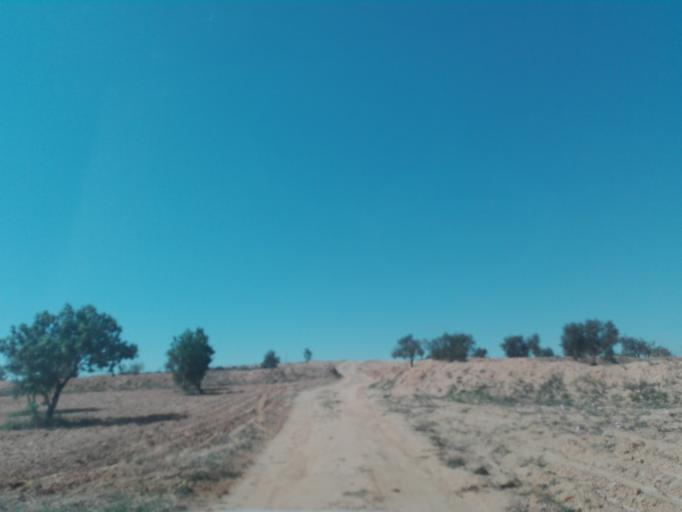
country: TN
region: Safaqis
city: Bi'r `Ali Bin Khalifah
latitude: 34.7954
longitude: 10.2831
